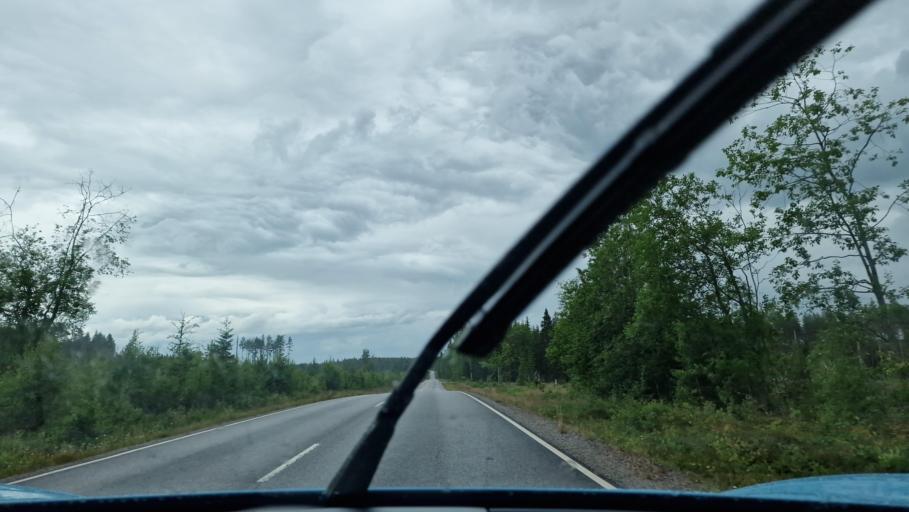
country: FI
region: Central Finland
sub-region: Saarijaervi-Viitasaari
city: Pylkoenmaeki
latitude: 62.6026
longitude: 24.5861
